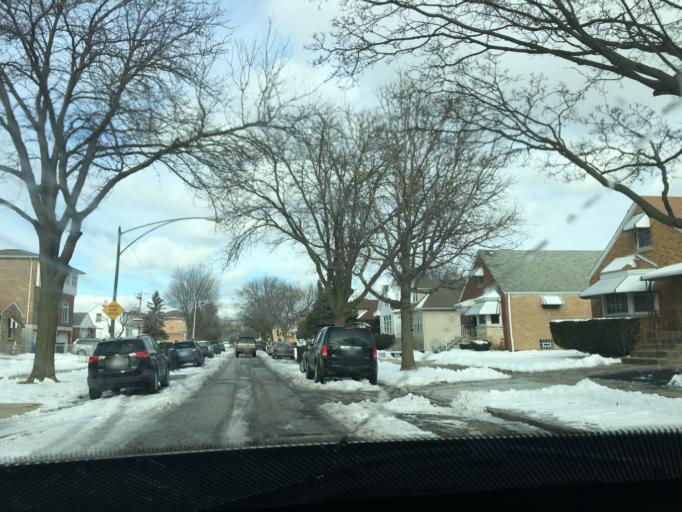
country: US
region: Illinois
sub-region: Cook County
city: Elmwood Park
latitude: 41.9365
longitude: -87.8128
